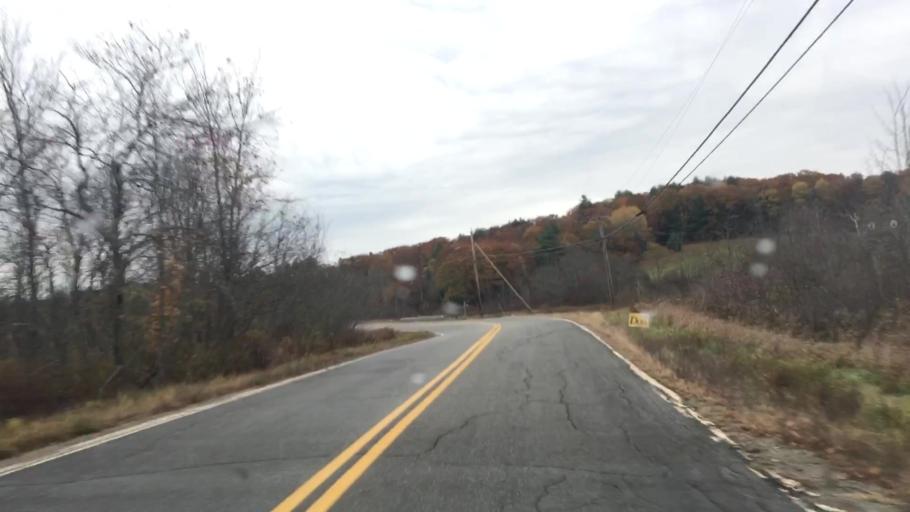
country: US
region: Maine
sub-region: Lincoln County
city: Whitefield
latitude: 44.1689
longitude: -69.6330
